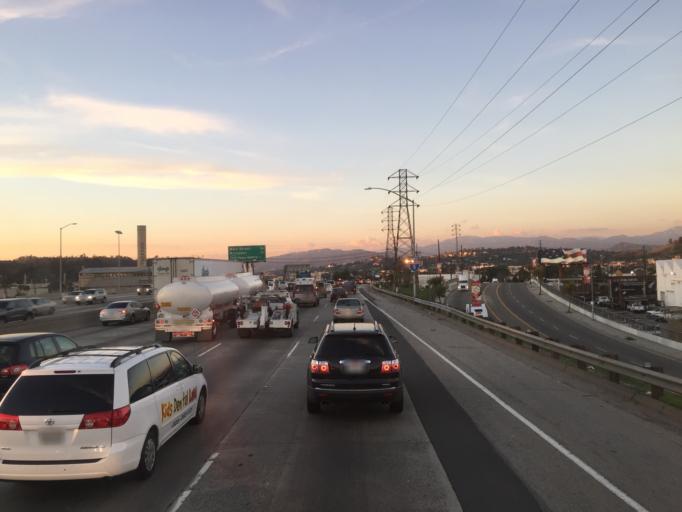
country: US
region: California
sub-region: Los Angeles County
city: Boyle Heights
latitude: 34.0614
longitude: -118.2152
